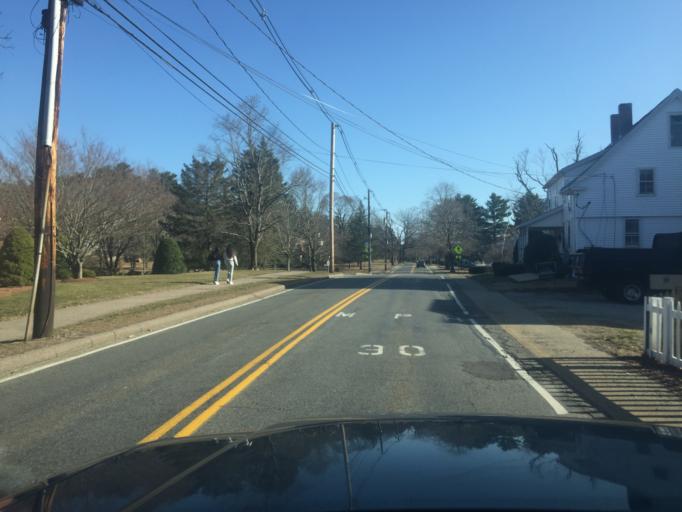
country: US
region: Massachusetts
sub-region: Norfolk County
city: Millis-Clicquot
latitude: 42.1650
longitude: -71.3555
